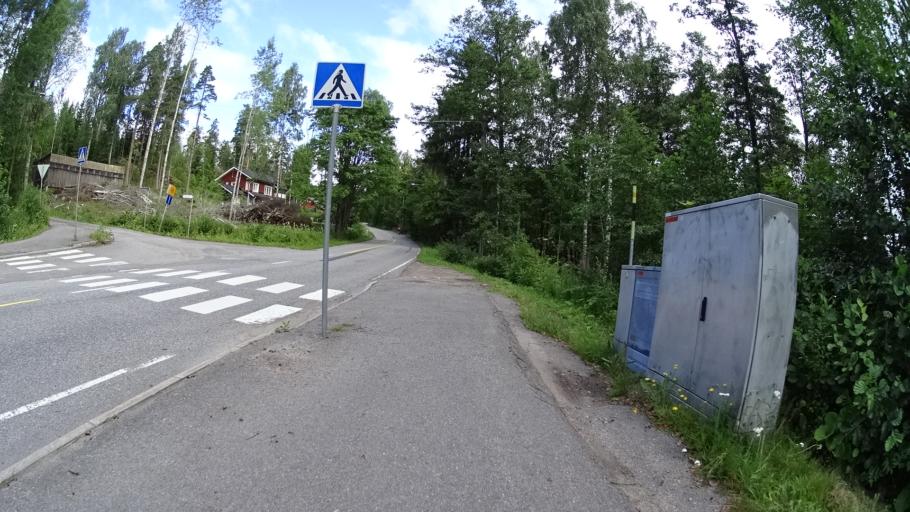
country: FI
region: Uusimaa
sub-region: Helsinki
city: Espoo
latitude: 60.2503
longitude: 24.6550
